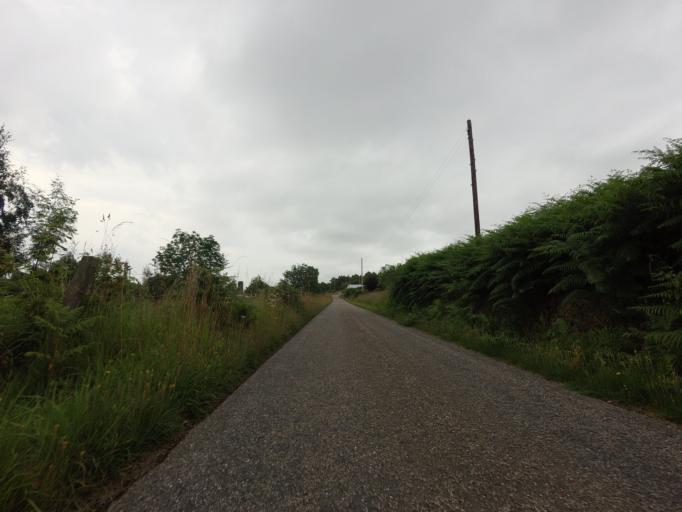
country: GB
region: Scotland
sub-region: Highland
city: Evanton
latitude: 57.9040
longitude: -4.3881
